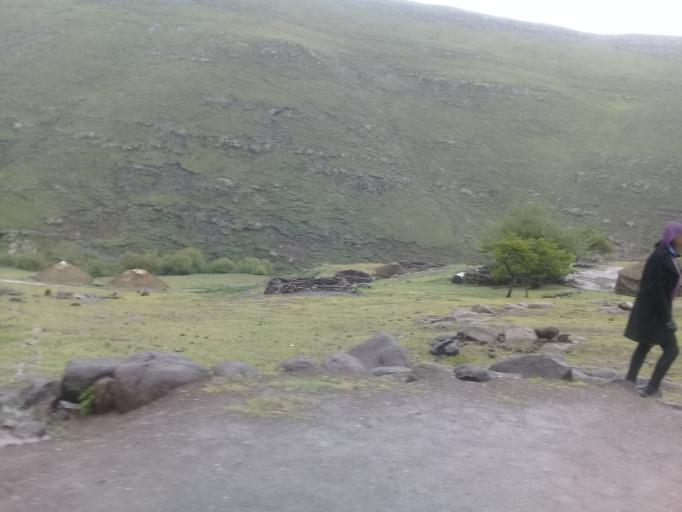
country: LS
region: Mokhotlong
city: Mokhotlong
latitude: -29.3873
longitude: 28.9532
